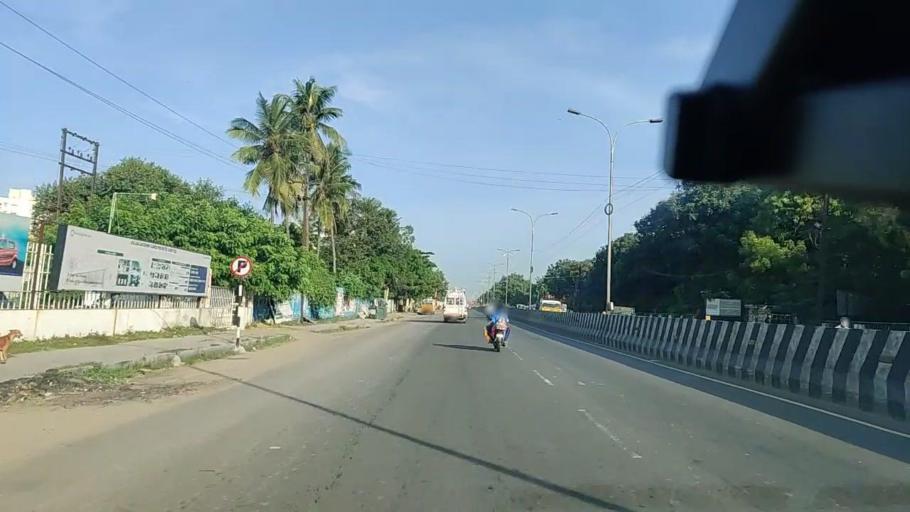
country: IN
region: Tamil Nadu
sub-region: Thiruvallur
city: Chinnasekkadu
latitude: 13.1374
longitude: 80.2298
